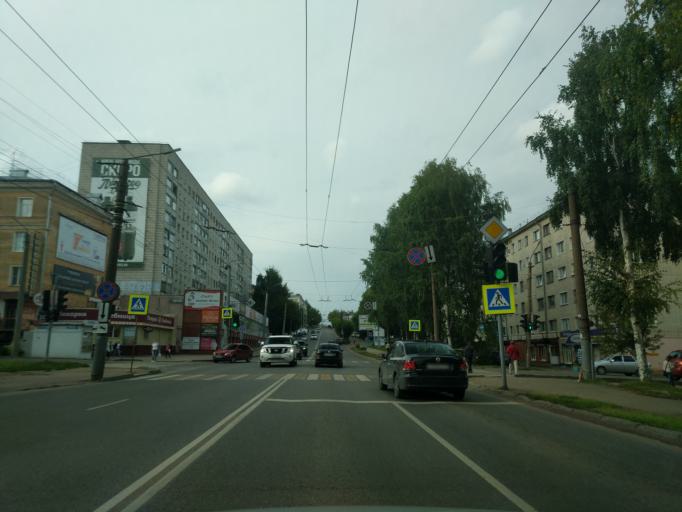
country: RU
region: Kirov
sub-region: Kirovo-Chepetskiy Rayon
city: Kirov
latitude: 58.5890
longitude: 49.6694
